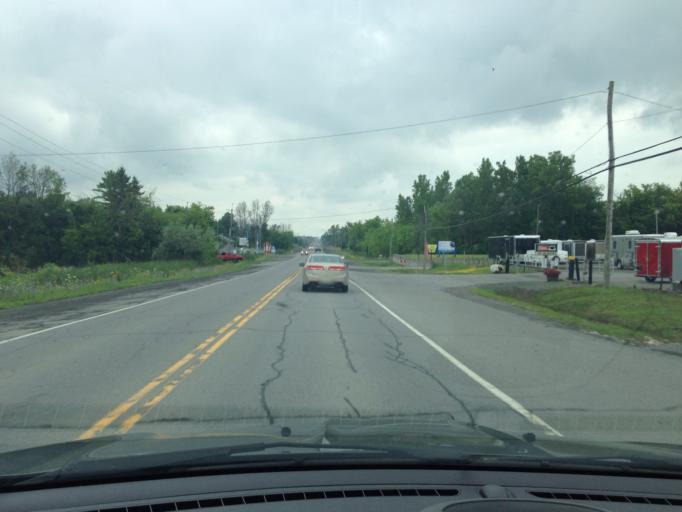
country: CA
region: Ontario
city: Ottawa
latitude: 45.3058
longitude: -75.5851
